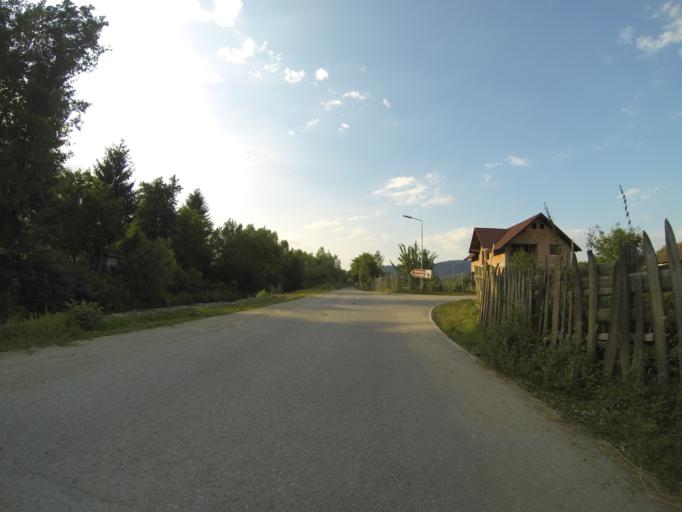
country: RO
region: Brasov
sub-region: Comuna Sinca Noua
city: Sinca Noua
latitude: 45.7081
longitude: 25.2457
